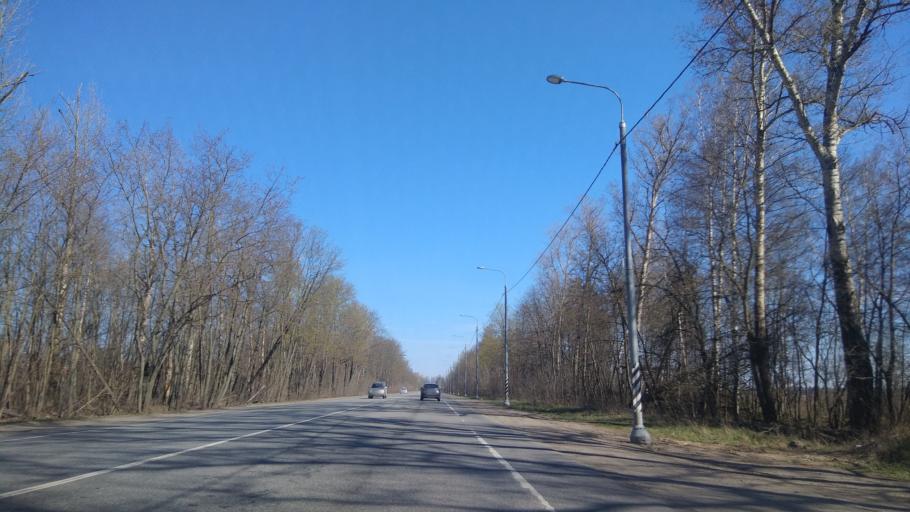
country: RU
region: Moskovskaya
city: Pushkino
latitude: 56.0345
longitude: 37.8706
